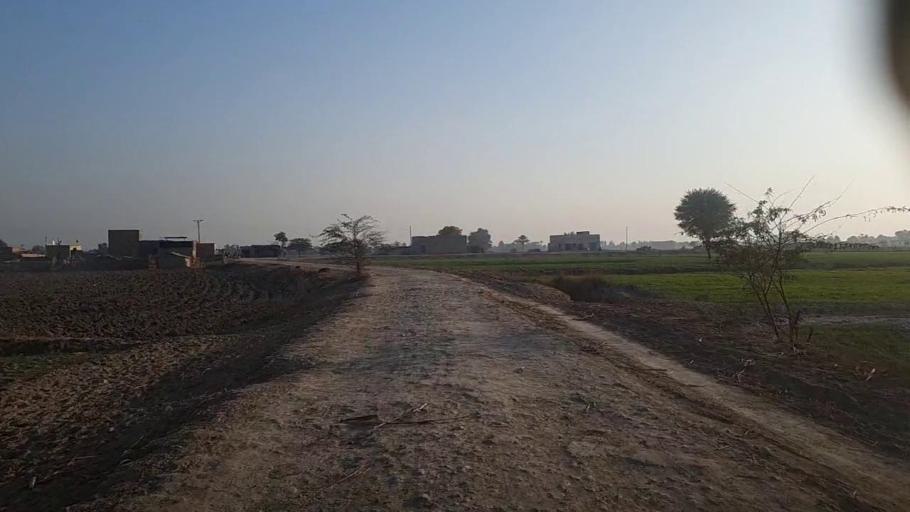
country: PK
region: Sindh
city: Khairpur
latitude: 28.0659
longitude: 69.7521
